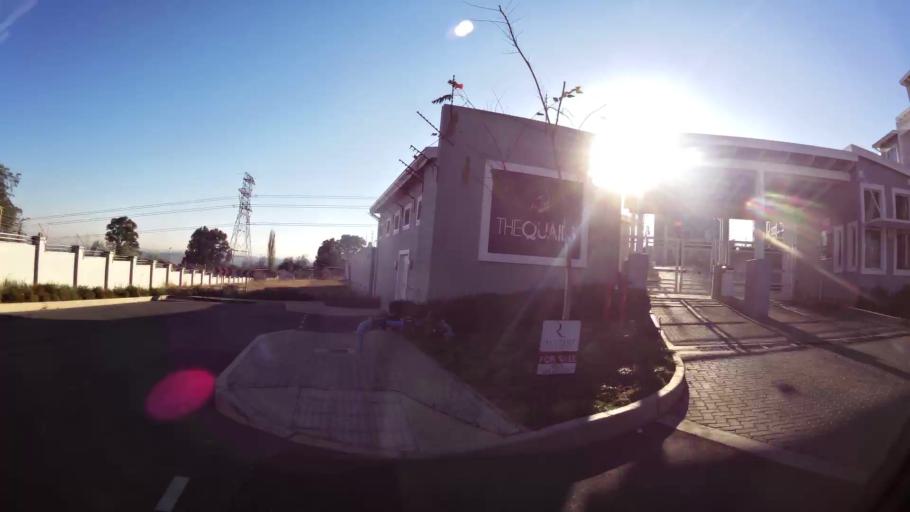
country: ZA
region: Gauteng
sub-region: City of Johannesburg Metropolitan Municipality
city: Midrand
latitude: -26.0260
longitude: 28.0409
